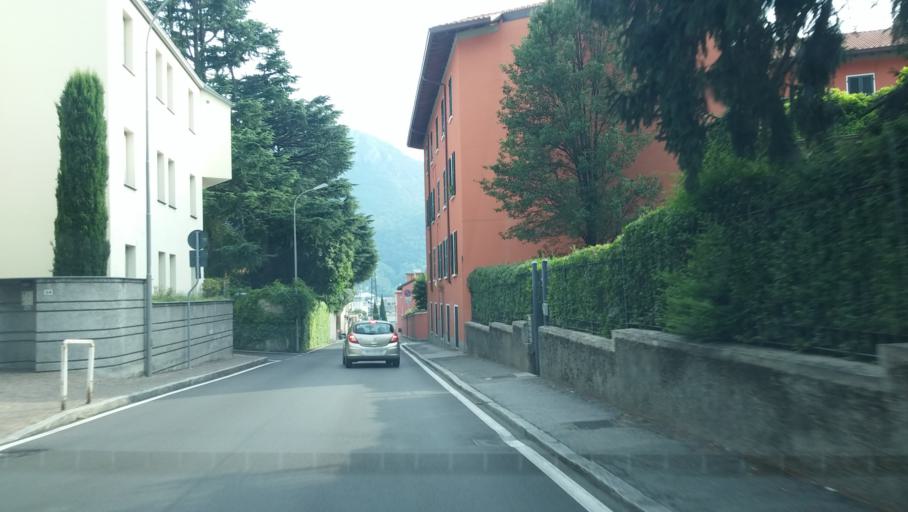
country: IT
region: Lombardy
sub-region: Provincia di Lecco
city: Lecco
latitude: 45.8601
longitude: 9.3922
